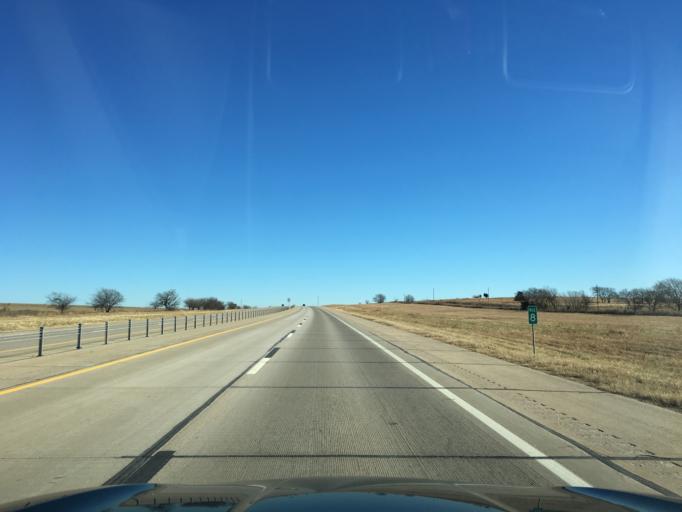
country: US
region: Oklahoma
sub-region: Noble County
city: Perry
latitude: 36.3922
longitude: -97.1866
